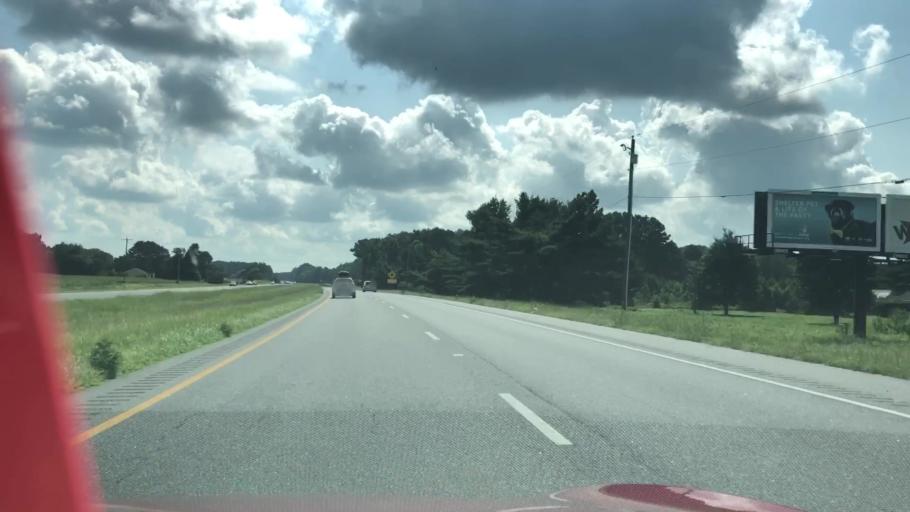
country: US
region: Maryland
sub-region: Somerset County
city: Princess Anne
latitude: 38.1212
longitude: -75.6824
